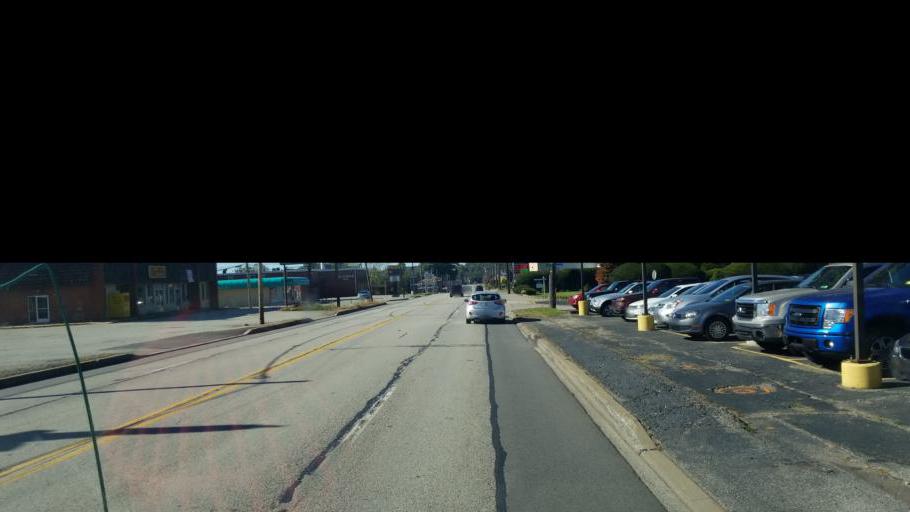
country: US
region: Pennsylvania
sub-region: Allegheny County
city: East McKeesport
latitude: 40.3780
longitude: -79.8031
